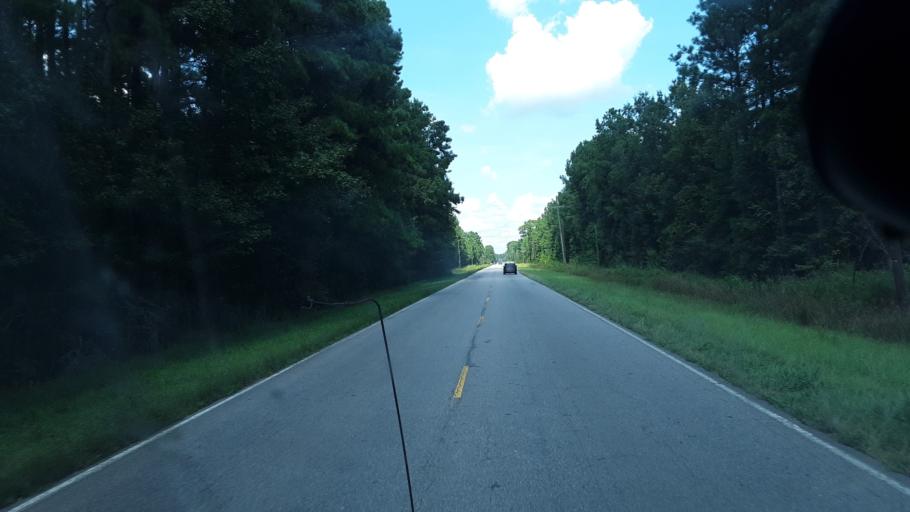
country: US
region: South Carolina
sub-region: Williamsburg County
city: Andrews
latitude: 33.3321
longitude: -79.6628
